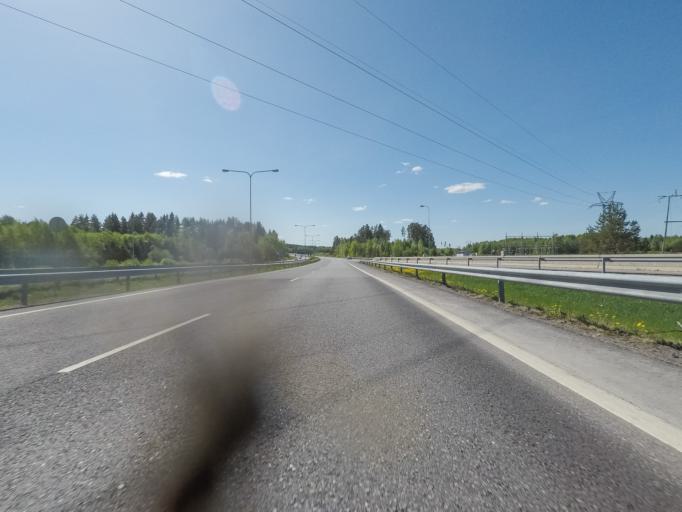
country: FI
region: Pirkanmaa
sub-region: Etelae-Pirkanmaa
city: Toijala
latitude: 61.2028
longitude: 23.8357
